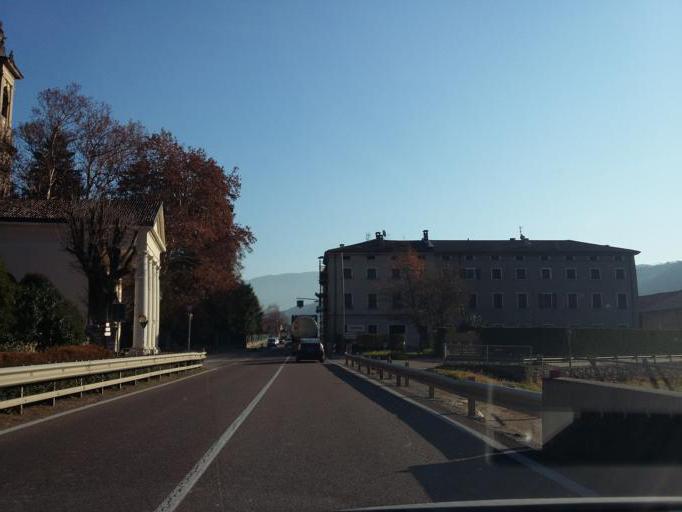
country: IT
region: Trentino-Alto Adige
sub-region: Provincia di Trento
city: Ronzo-Chienis
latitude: 45.8561
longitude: 10.9276
